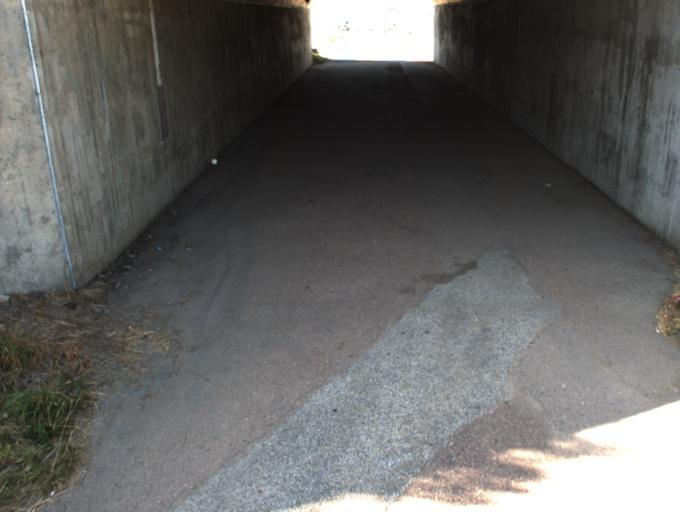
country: SE
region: Skane
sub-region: Helsingborg
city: Odakra
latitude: 56.0898
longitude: 12.7591
